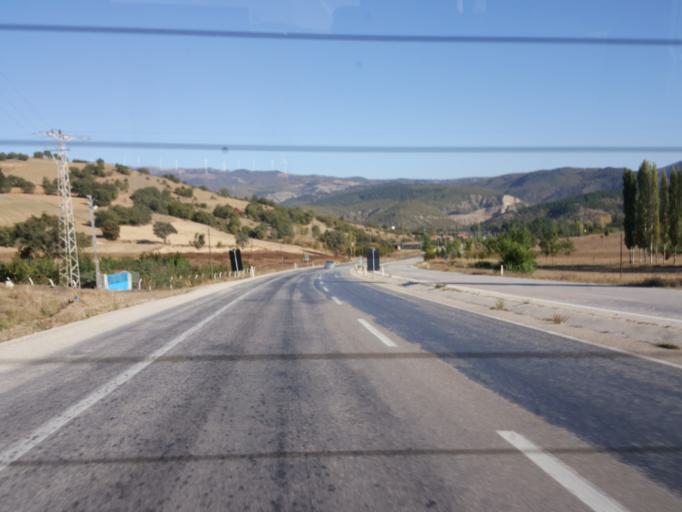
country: TR
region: Amasya
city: Ezinepazari
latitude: 40.5579
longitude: 36.1381
